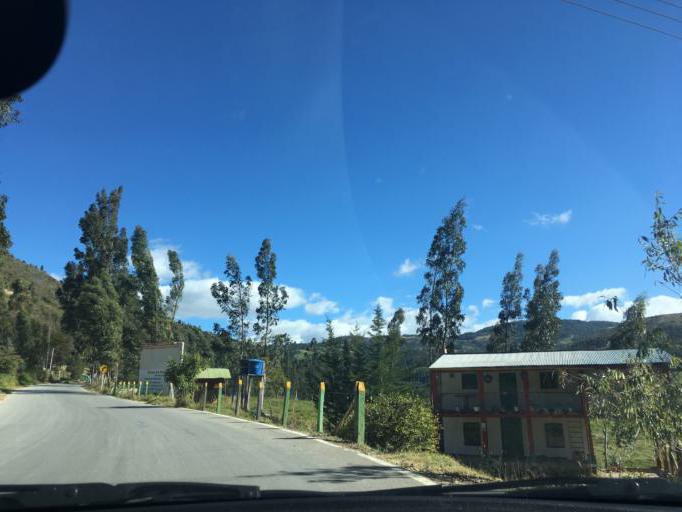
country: CO
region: Boyaca
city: Firavitoba
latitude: 5.5920
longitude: -72.9781
